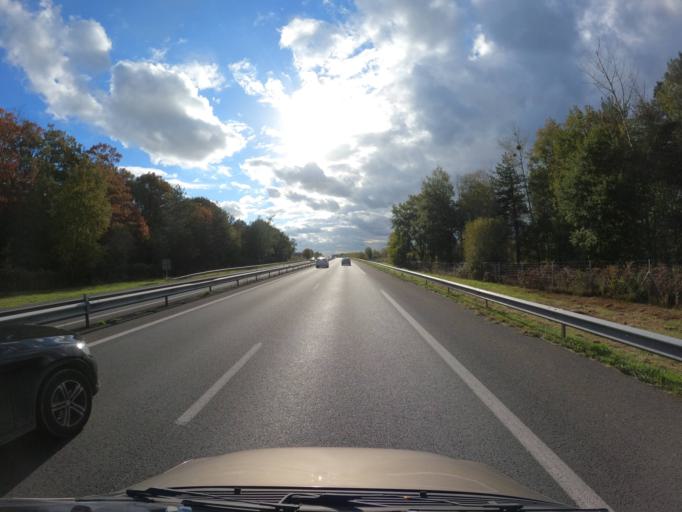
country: FR
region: Pays de la Loire
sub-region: Departement de la Sarthe
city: Louplande
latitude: 47.9187
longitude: -0.0779
